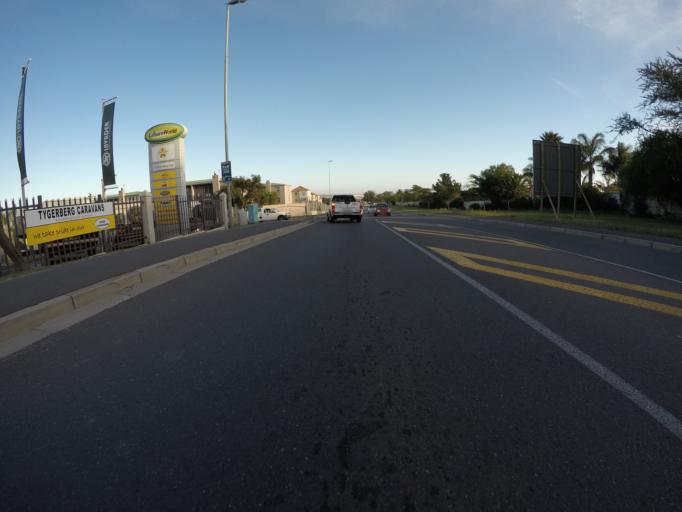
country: ZA
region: Western Cape
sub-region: City of Cape Town
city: Kraaifontein
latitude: -33.8616
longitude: 18.6832
